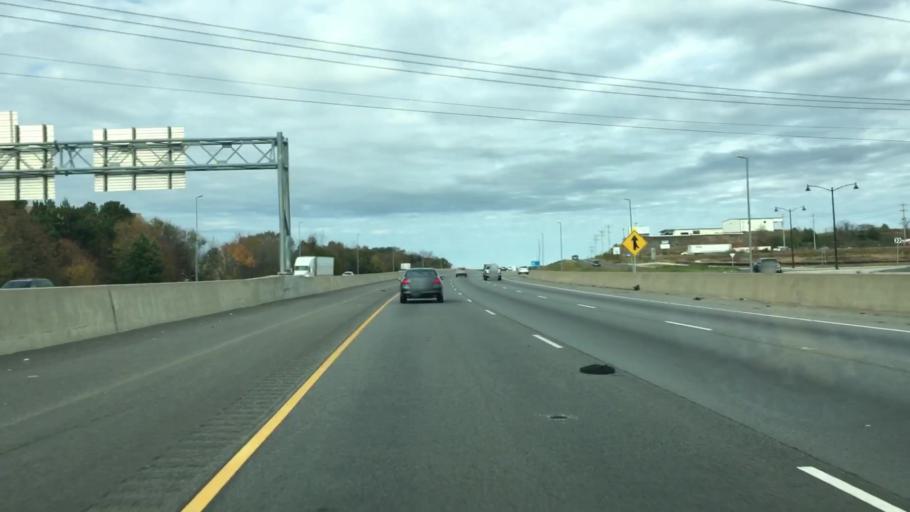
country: US
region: Arkansas
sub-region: Faulkner County
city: Conway
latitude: 35.0707
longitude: -92.4170
